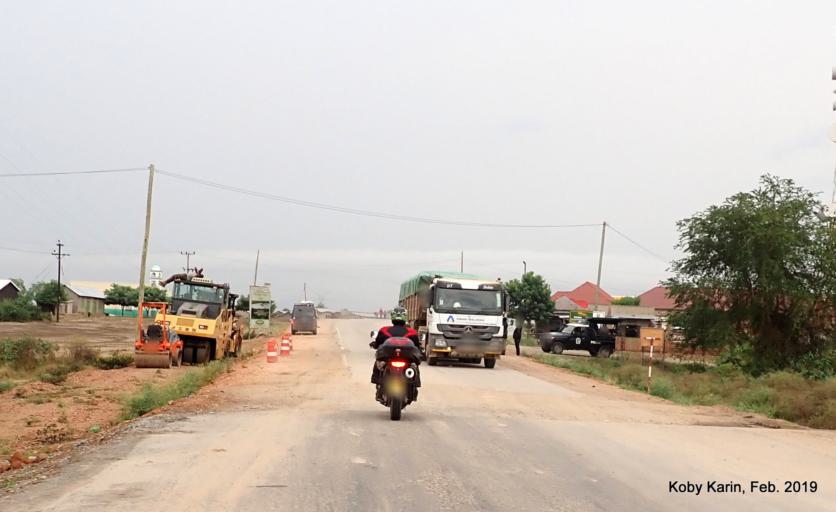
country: UG
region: Western Region
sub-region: Rubirizi District
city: Rubirizi
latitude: -0.1186
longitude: 30.0472
